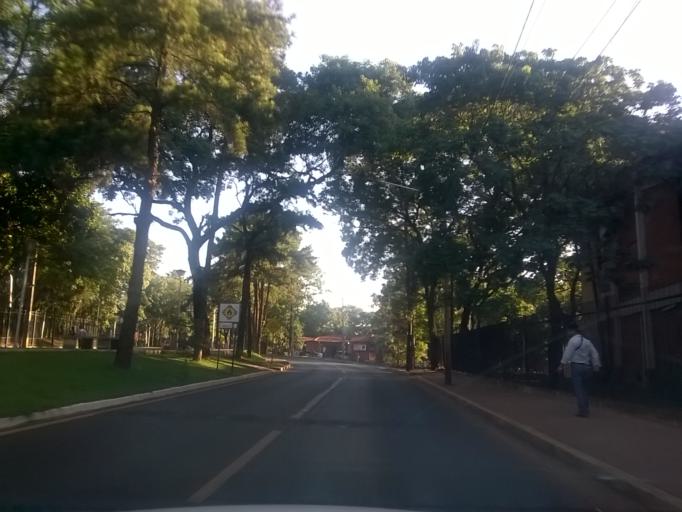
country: PY
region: Alto Parana
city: Ciudad del Este
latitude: -25.5148
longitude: -54.6157
